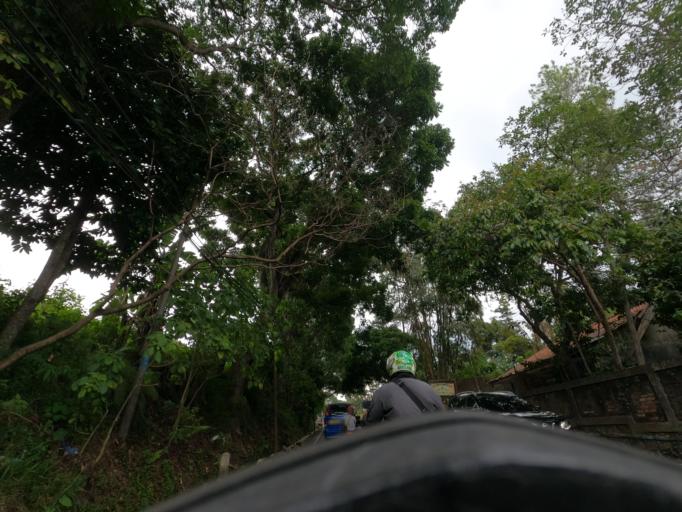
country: ID
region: West Java
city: Sukabumi
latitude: -6.7846
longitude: 107.0638
